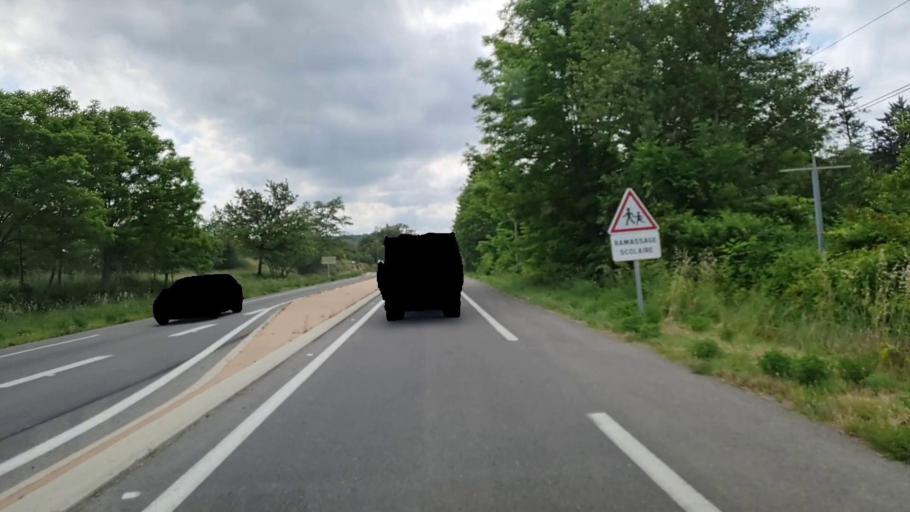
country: FR
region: Languedoc-Roussillon
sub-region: Departement du Gard
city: Sauve
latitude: 43.9334
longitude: 3.9762
